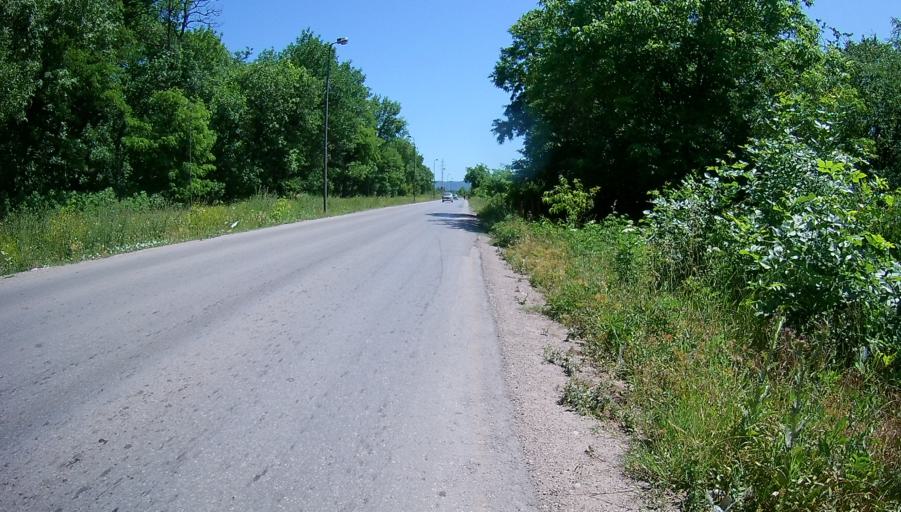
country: RS
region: Central Serbia
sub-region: Nisavski Okrug
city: Nis
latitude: 43.2996
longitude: 21.8759
